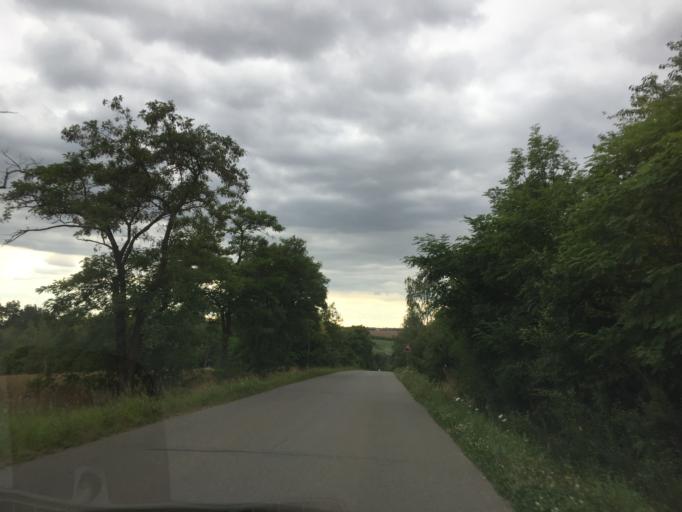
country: DE
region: Thuringia
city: Schmolln
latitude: 50.8762
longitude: 12.3387
